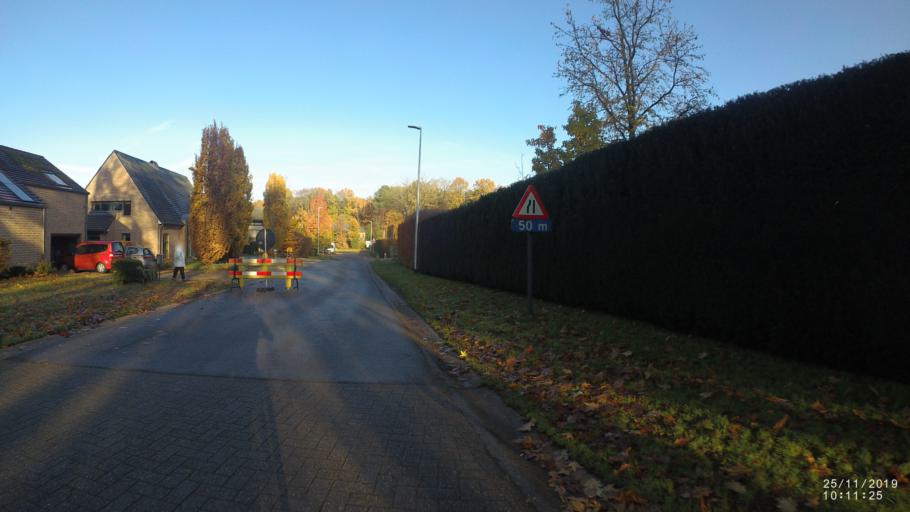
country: BE
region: Flanders
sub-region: Provincie Vlaams-Brabant
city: Diest
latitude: 50.9959
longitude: 5.0247
